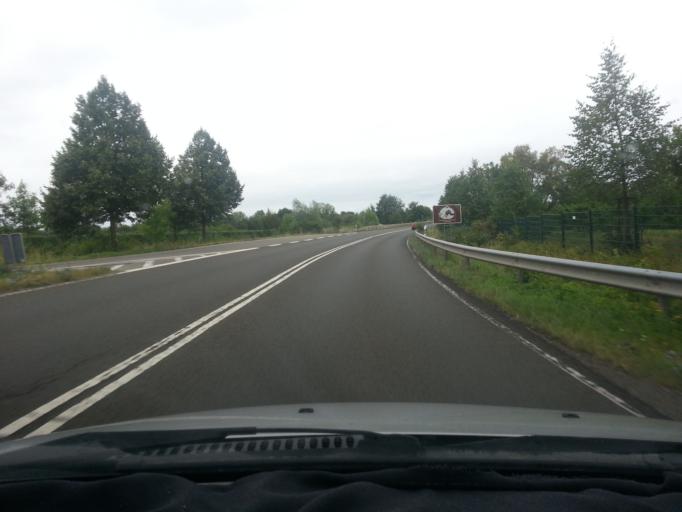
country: DE
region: Rheinland-Pfalz
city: Wachenheim
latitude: 49.4486
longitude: 8.1979
